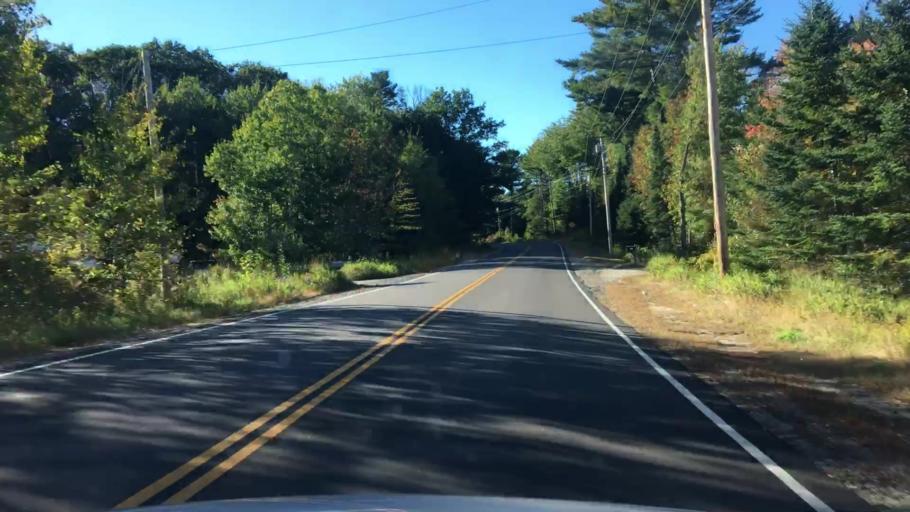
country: US
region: Maine
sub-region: Androscoggin County
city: Lisbon
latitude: 44.0740
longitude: -70.0987
